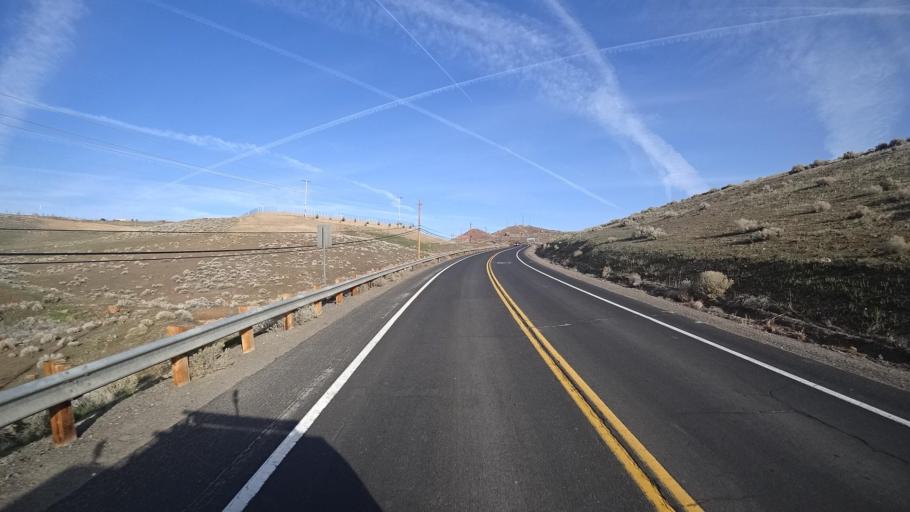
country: US
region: Nevada
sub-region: Washoe County
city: Sun Valley
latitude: 39.5721
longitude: -119.7881
